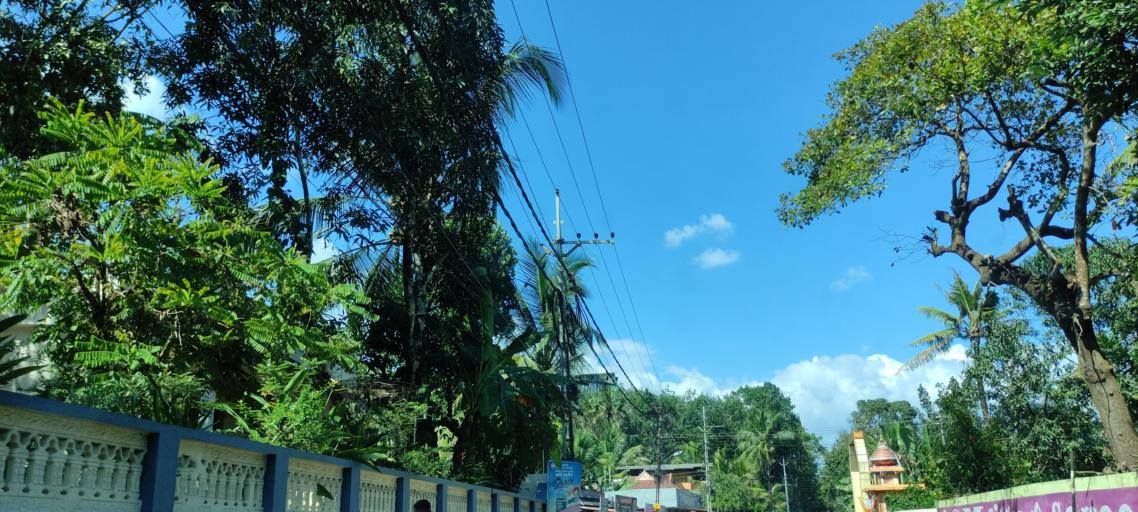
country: IN
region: Kerala
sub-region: Pattanamtitta
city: Adur
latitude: 9.1683
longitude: 76.7412
